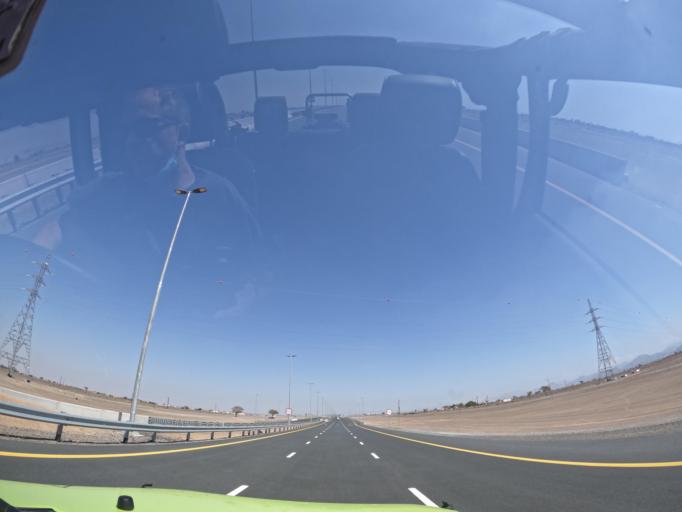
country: AE
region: Ash Shariqah
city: Adh Dhayd
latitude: 25.1012
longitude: 55.9282
